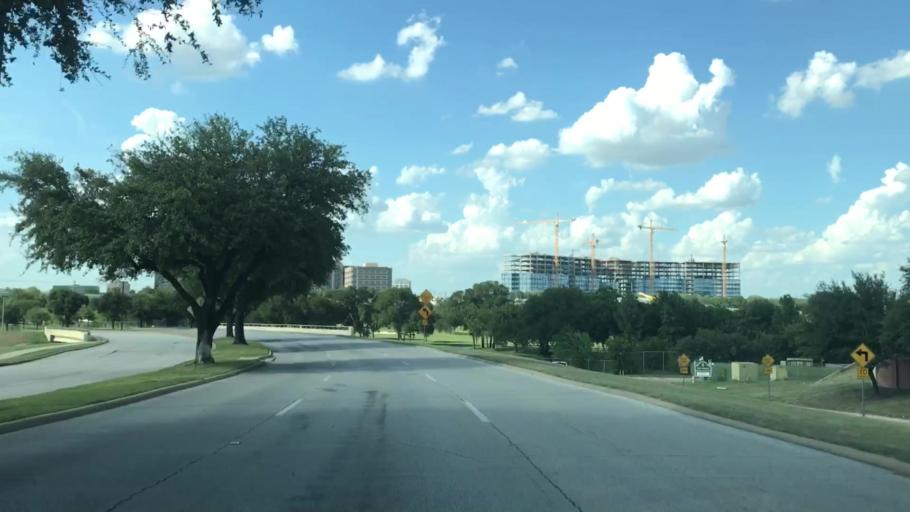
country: US
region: Texas
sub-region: Dallas County
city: Irving
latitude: 32.8716
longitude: -96.9587
